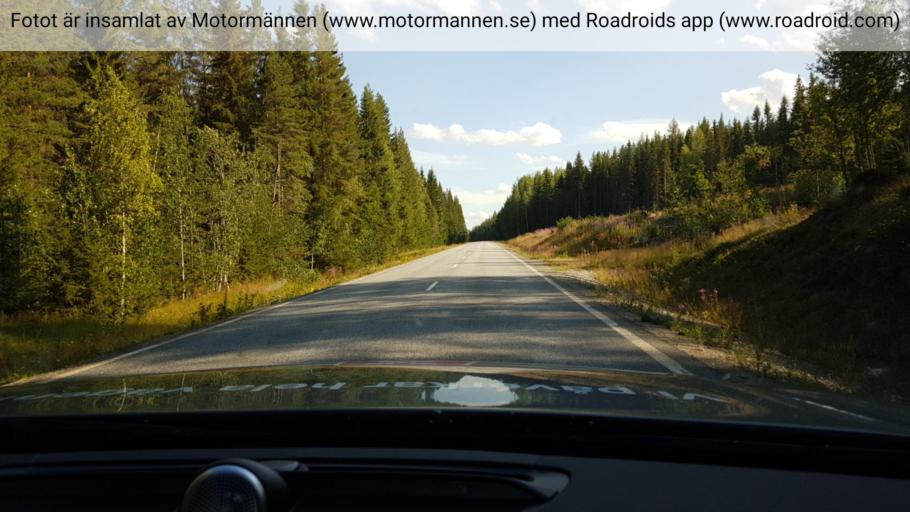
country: SE
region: Vaesterbotten
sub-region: Dorotea Kommun
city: Dorotea
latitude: 63.8770
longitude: 16.3739
